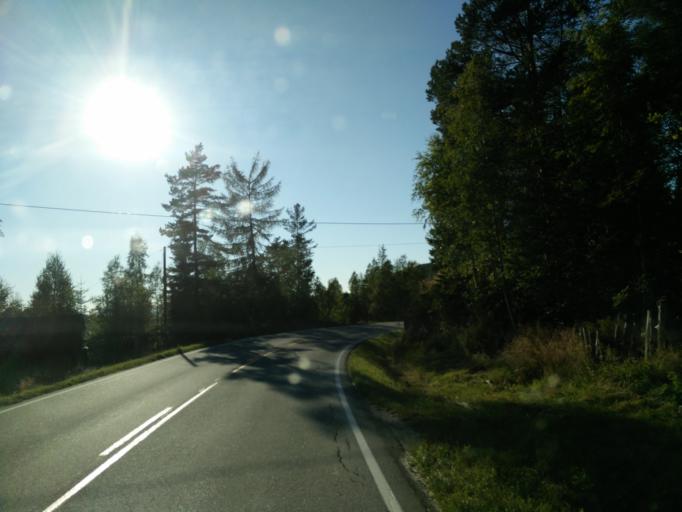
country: NO
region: More og Romsdal
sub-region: Halsa
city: Liaboen
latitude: 63.0847
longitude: 8.3962
